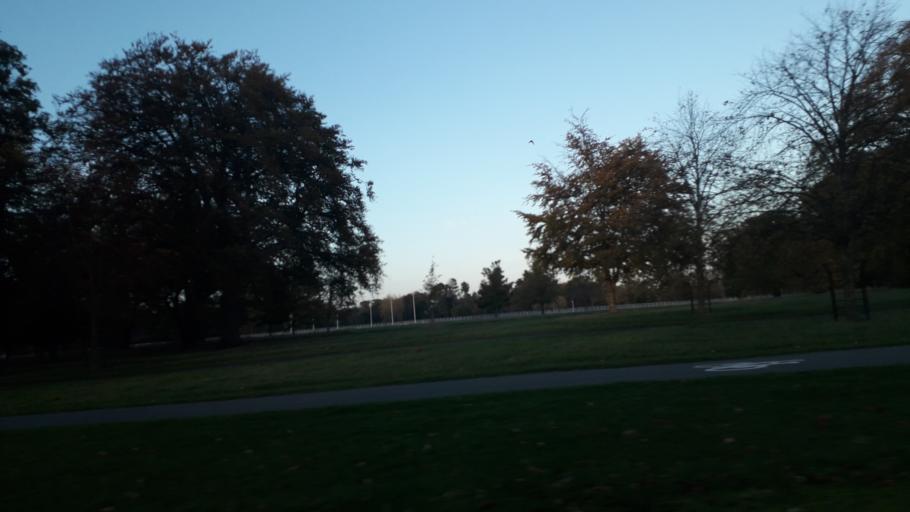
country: IE
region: Leinster
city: Chapelizod
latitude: 53.3623
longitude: -6.3310
